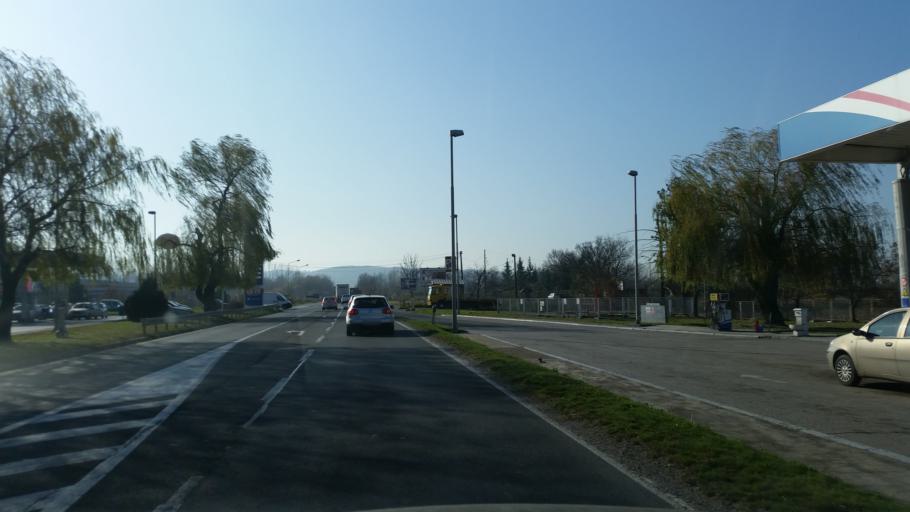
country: RS
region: Central Serbia
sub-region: Belgrade
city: Lazarevac
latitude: 44.3914
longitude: 20.2398
